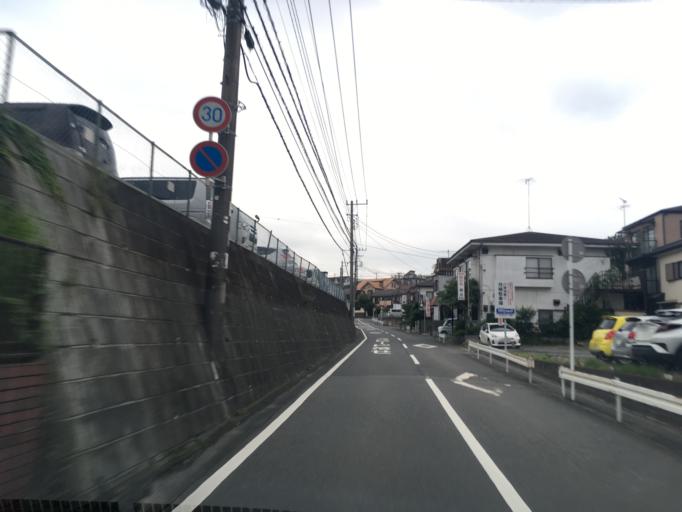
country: JP
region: Saitama
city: Sayama
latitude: 35.8312
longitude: 139.3670
